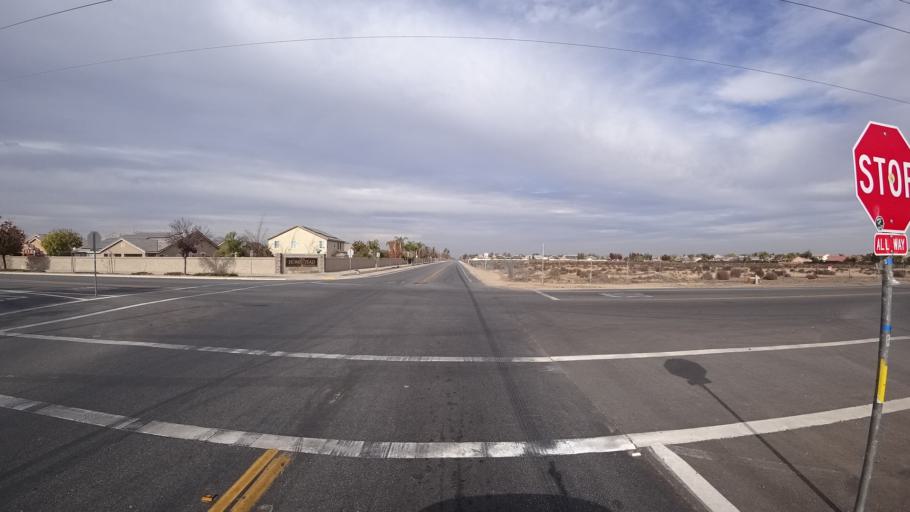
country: US
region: California
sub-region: Kern County
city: Rosedale
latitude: 35.4050
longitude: -119.1367
